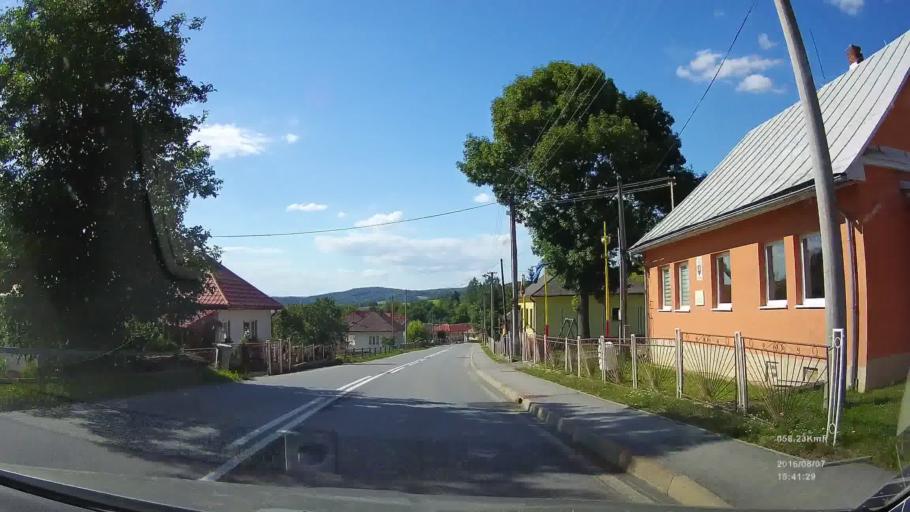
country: SK
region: Presovsky
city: Giraltovce
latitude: 49.1248
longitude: 21.5774
